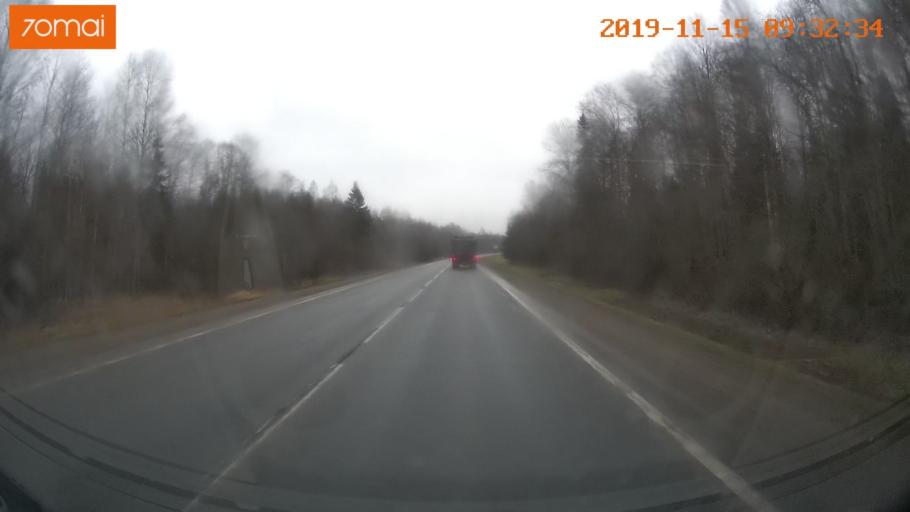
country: RU
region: Vologda
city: Sheksna
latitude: 59.2711
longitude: 38.3383
